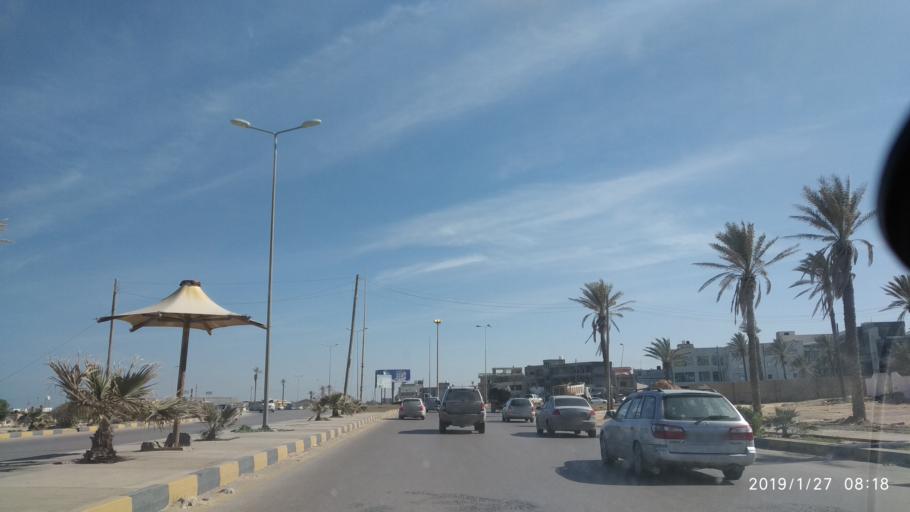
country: LY
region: Tripoli
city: Tagiura
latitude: 32.8944
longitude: 13.3417
